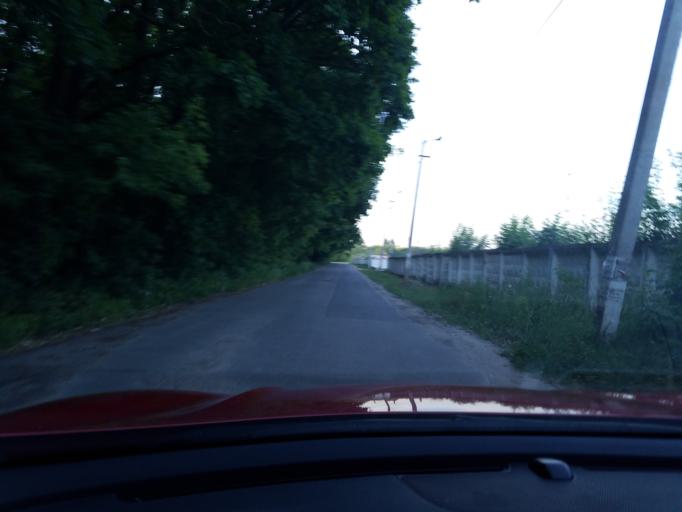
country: RU
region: Orjol
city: Znamenka
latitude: 52.9128
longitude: 36.0061
